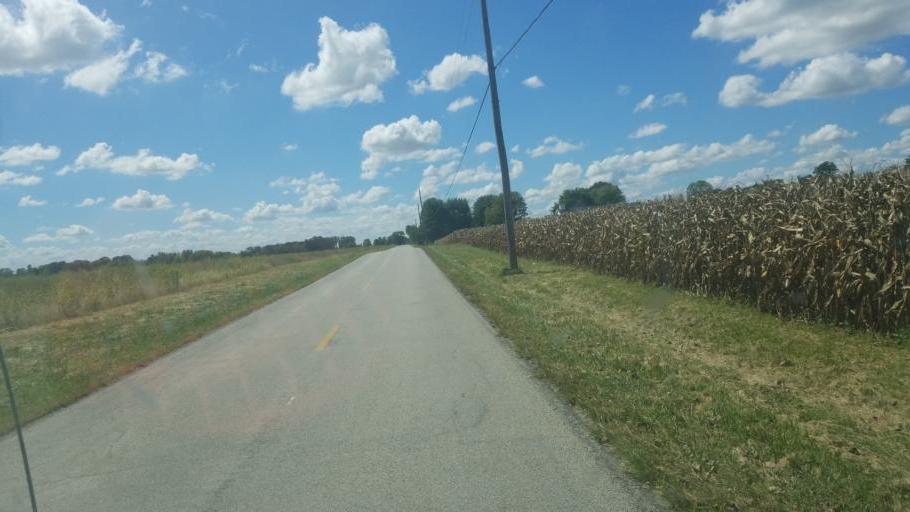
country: US
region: Ohio
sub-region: Madison County
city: West Jefferson
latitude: 39.9963
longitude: -83.2679
